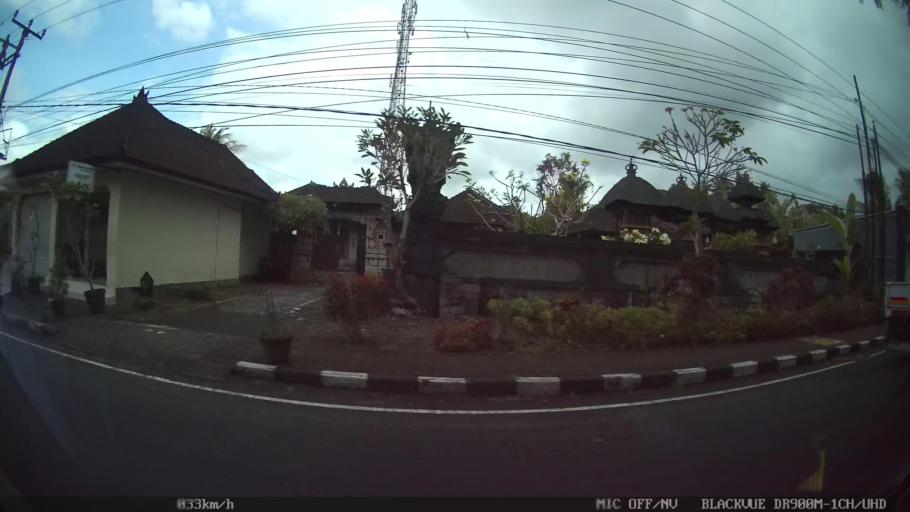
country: ID
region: Bali
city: Banjar Cemenggon
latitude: -8.5389
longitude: 115.1990
